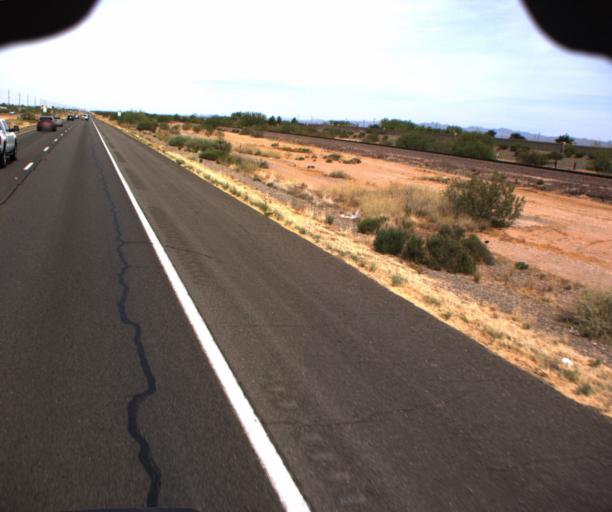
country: US
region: Arizona
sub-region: Maricopa County
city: Sun City West
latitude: 33.6962
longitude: -112.4237
